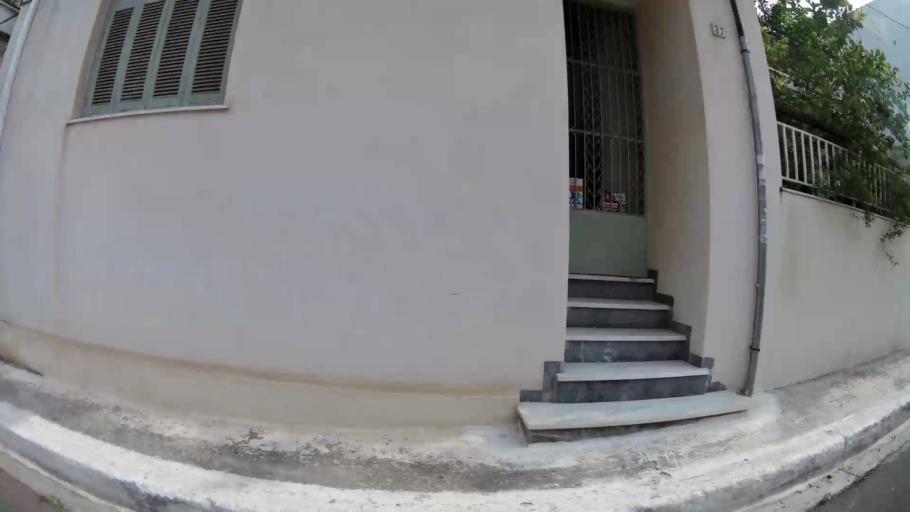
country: GR
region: Attica
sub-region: Nomarchia Athinas
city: Peristeri
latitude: 38.0102
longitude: 23.6851
